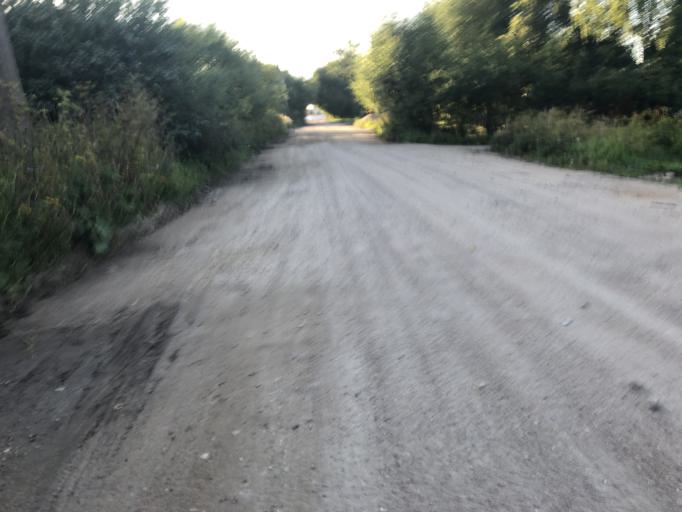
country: RU
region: Tverskaya
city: Rzhev
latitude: 56.2447
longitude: 34.3045
